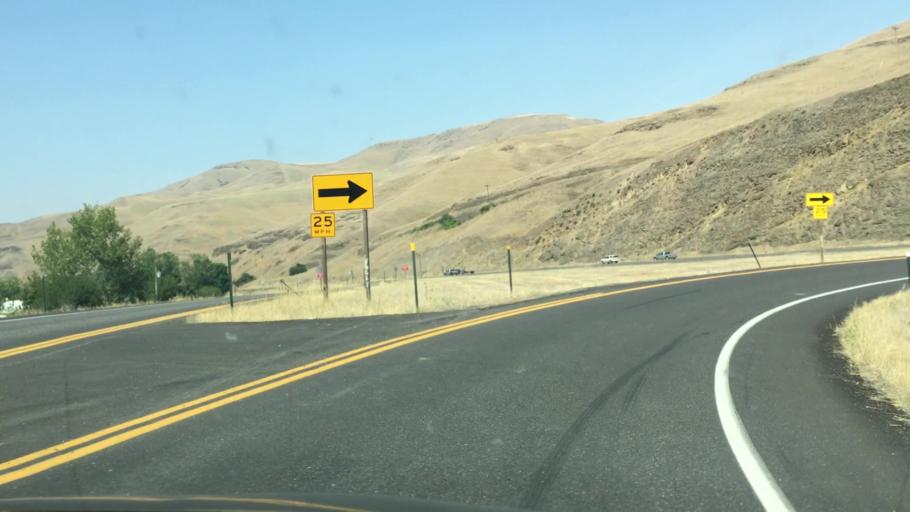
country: US
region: Idaho
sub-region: Nez Perce County
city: Lapwai
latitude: 46.4471
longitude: -116.8547
